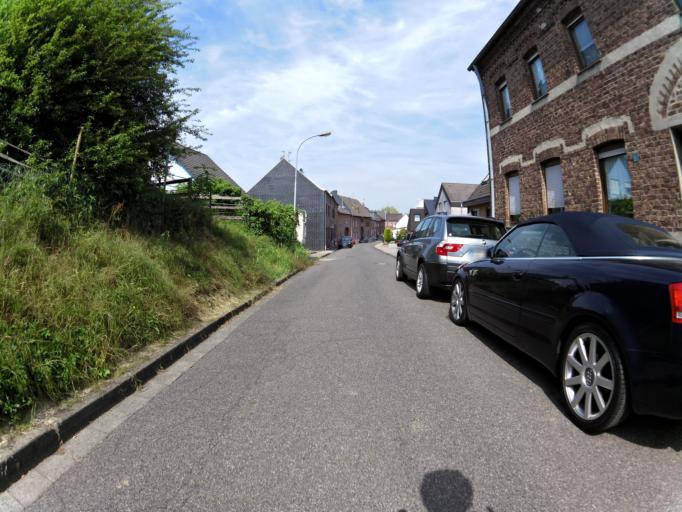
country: DE
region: North Rhine-Westphalia
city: Niedermerz
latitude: 50.9051
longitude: 6.2535
